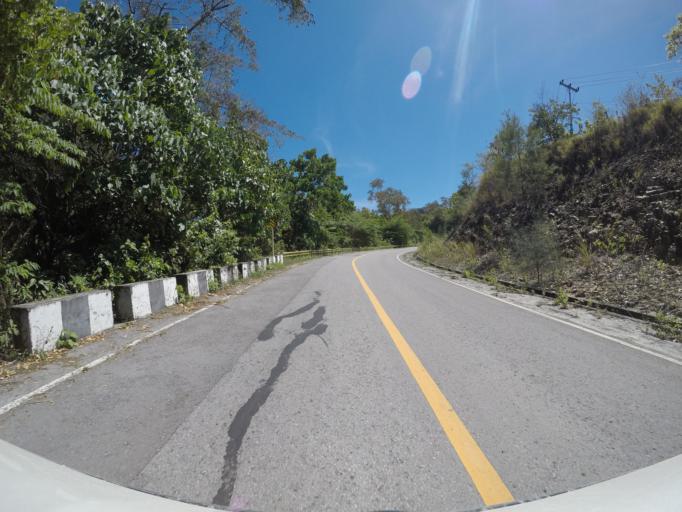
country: TL
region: Manatuto
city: Manatuto
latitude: -8.8152
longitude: 125.9734
